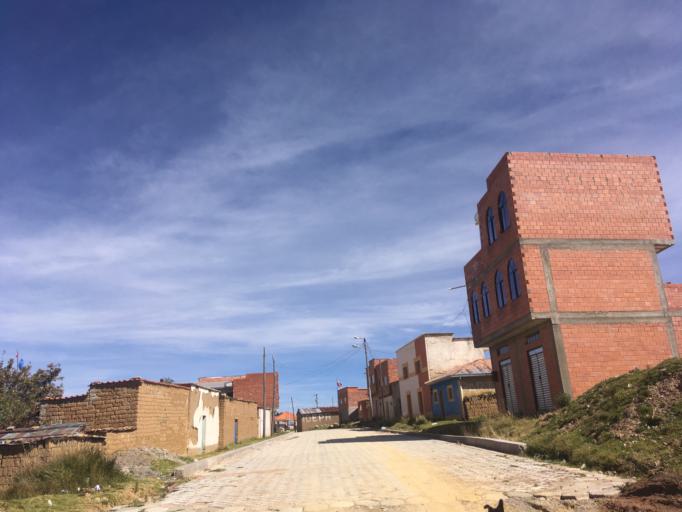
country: BO
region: La Paz
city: San Pedro
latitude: -16.2623
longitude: -68.8800
